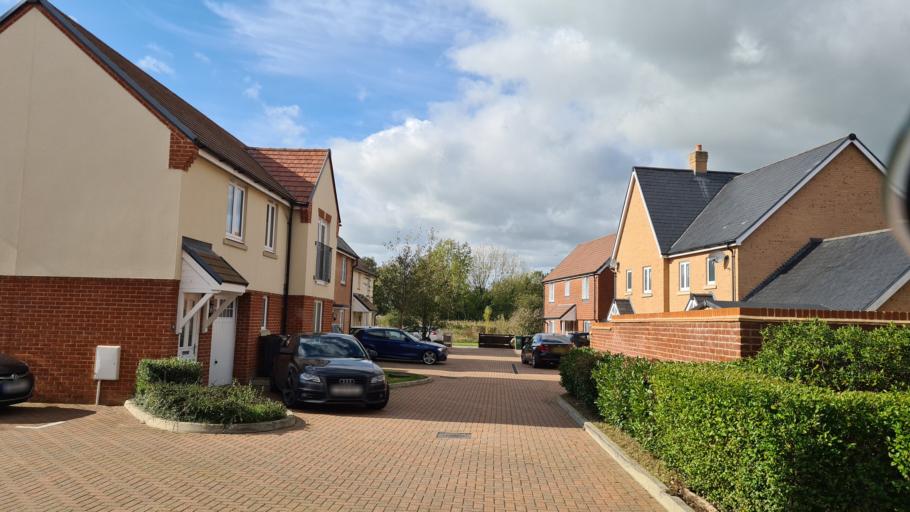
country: GB
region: England
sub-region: East Sussex
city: Hailsham
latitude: 50.8730
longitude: 0.2402
